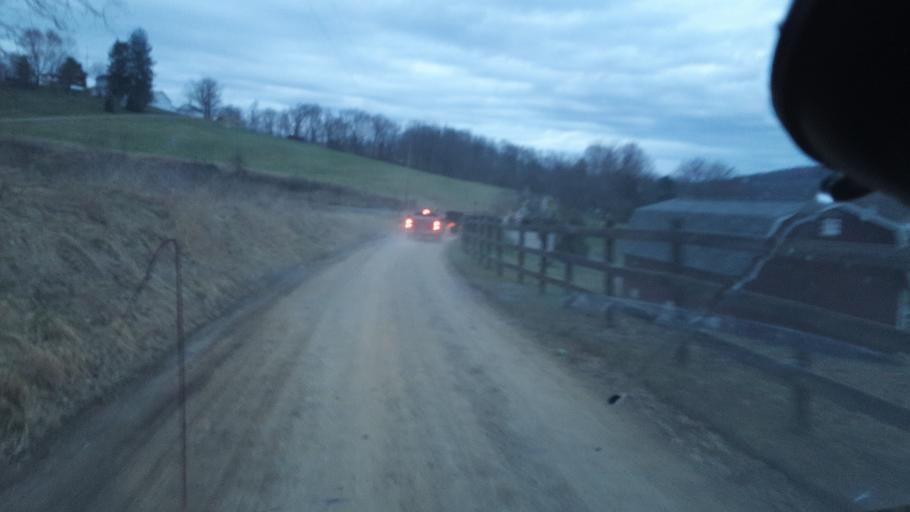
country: US
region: Ohio
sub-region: Coshocton County
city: West Lafayette
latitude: 40.3533
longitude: -81.7668
